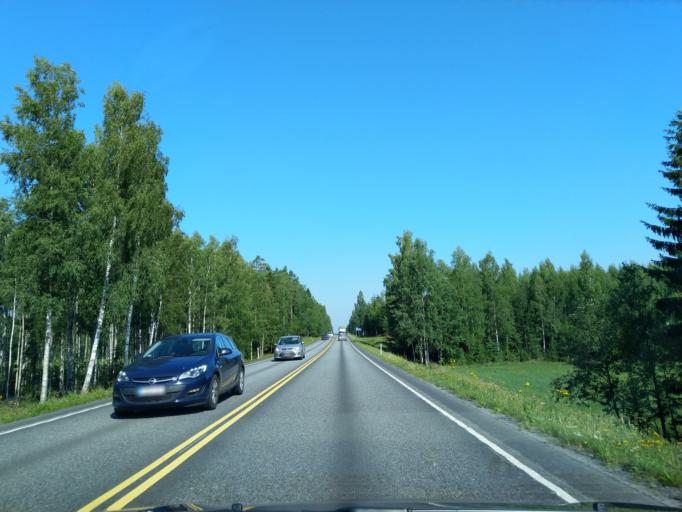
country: FI
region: Varsinais-Suomi
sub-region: Loimaa
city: Alastaro
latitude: 61.0760
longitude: 22.9119
